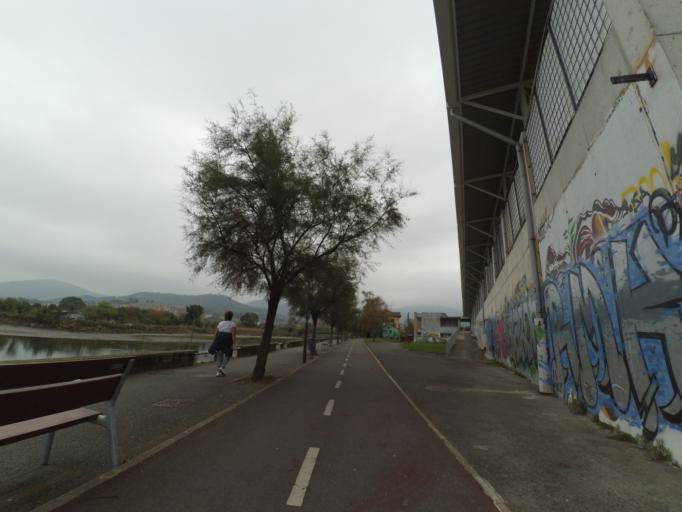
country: ES
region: Basque Country
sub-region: Provincia de Guipuzcoa
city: Irun
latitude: 43.3459
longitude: -1.7853
